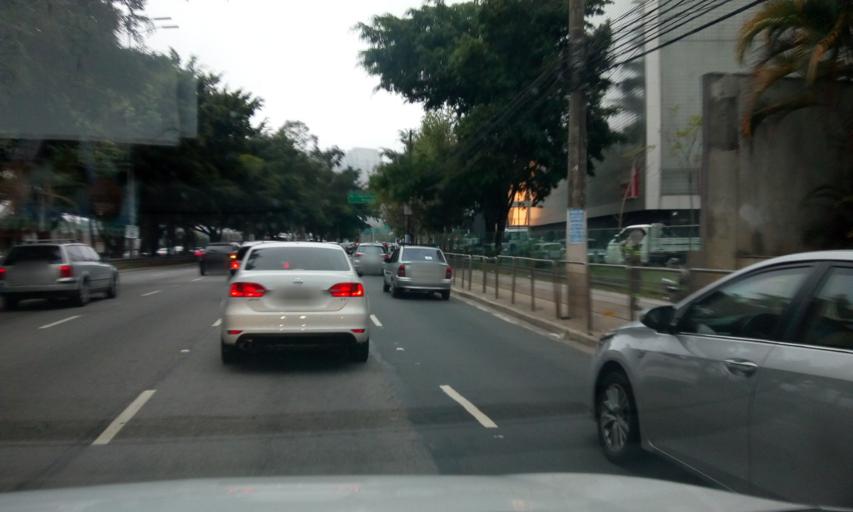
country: BR
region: Sao Paulo
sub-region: Sao Paulo
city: Sao Paulo
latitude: -23.5935
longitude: -46.6922
